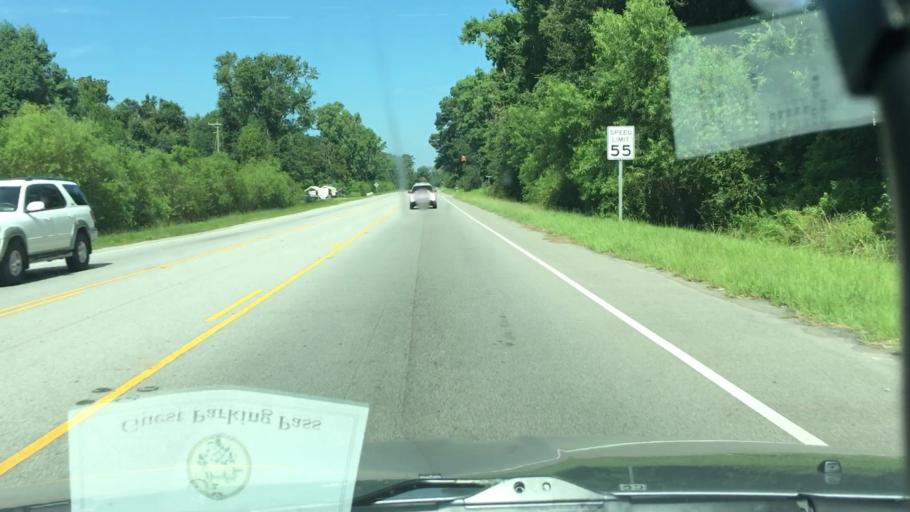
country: US
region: South Carolina
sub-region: Beaufort County
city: Beaufort
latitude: 32.3957
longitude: -80.5876
